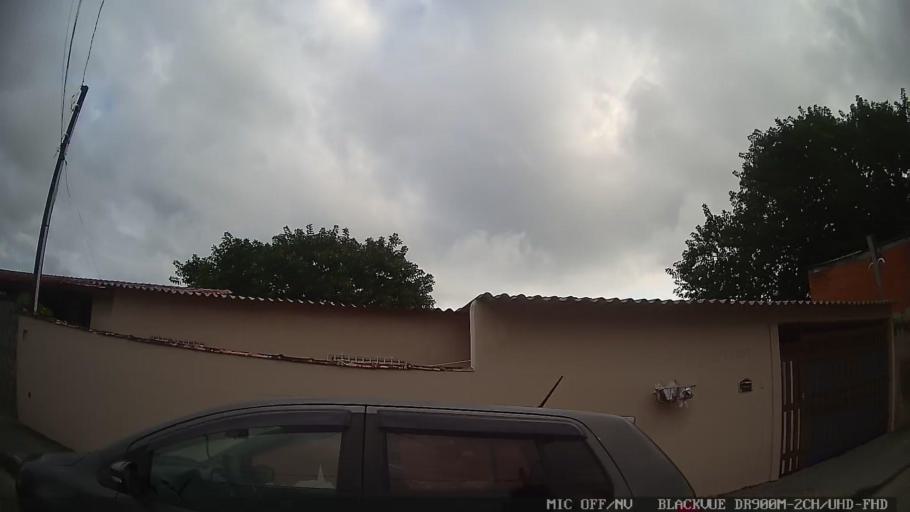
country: BR
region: Sao Paulo
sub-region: Itanhaem
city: Itanhaem
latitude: -24.1919
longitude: -46.8109
